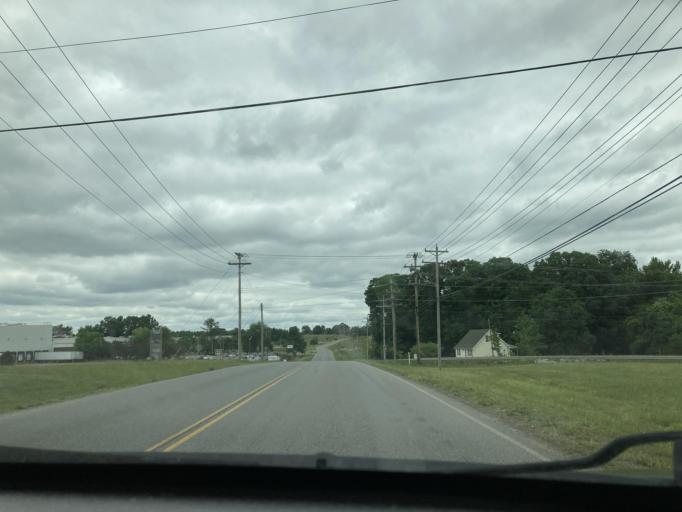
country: US
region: Tennessee
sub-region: Dickson County
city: Burns
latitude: 36.0451
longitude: -87.3430
